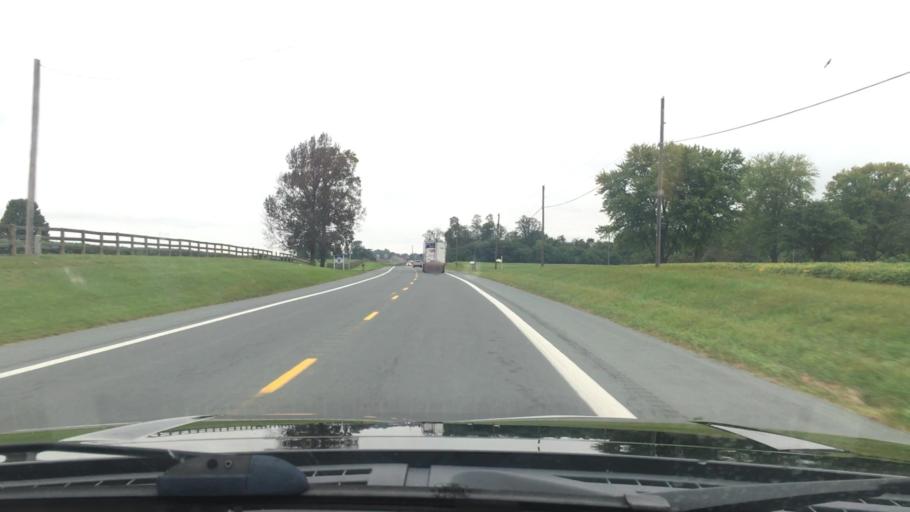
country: US
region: Maryland
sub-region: Cecil County
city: Elkton
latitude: 39.4792
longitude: -75.8481
